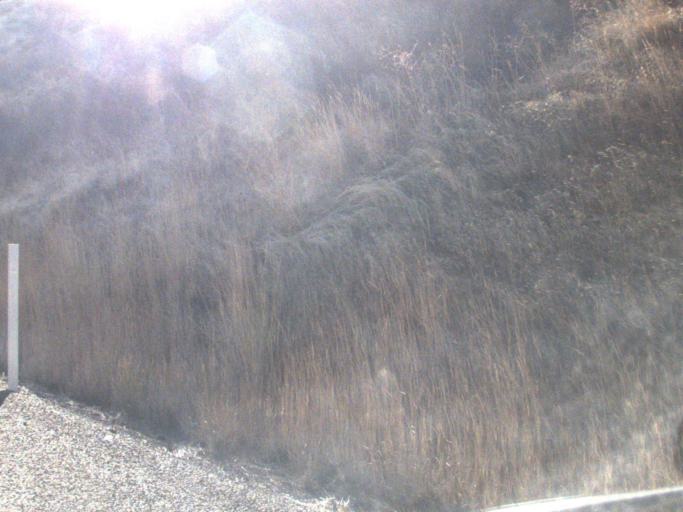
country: US
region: Washington
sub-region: Garfield County
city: Pomeroy
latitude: 46.4384
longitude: -117.3669
